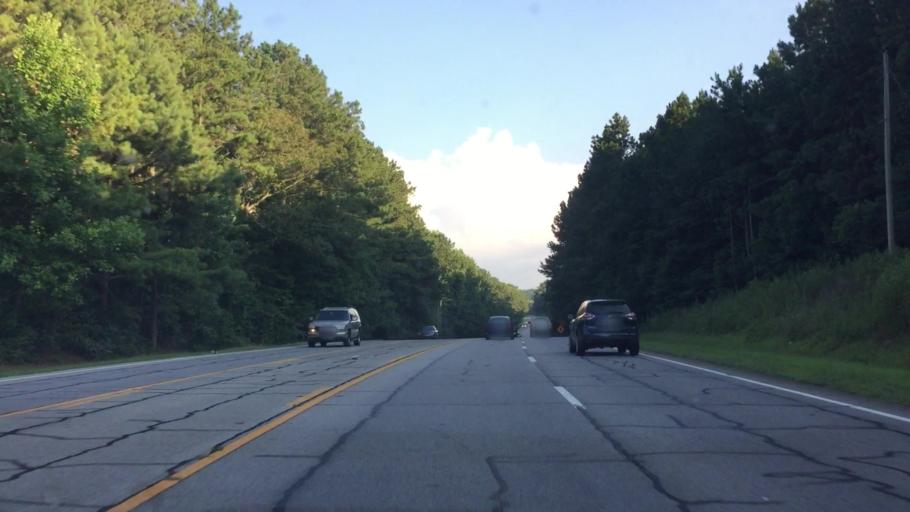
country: US
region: Georgia
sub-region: DeKalb County
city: Pine Mountain
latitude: 33.6424
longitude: -84.1859
